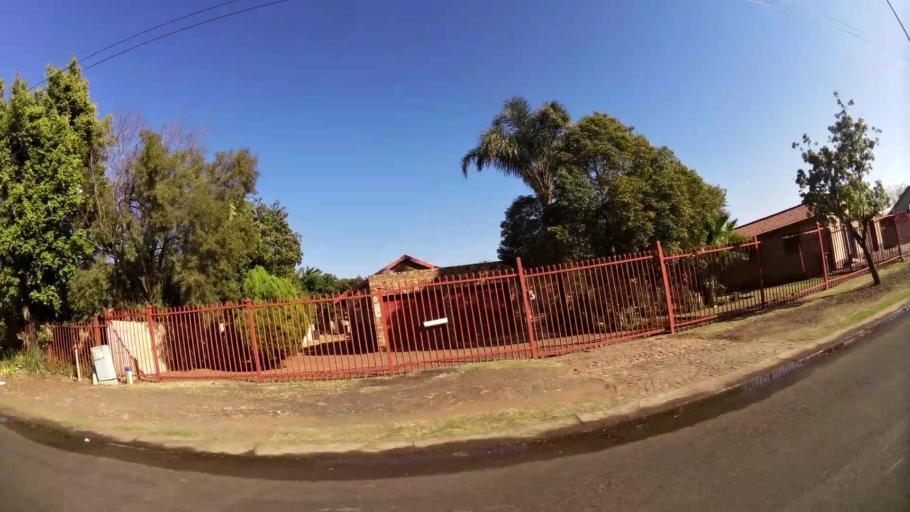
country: ZA
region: Gauteng
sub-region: City of Tshwane Metropolitan Municipality
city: Pretoria
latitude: -25.6645
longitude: 28.1429
